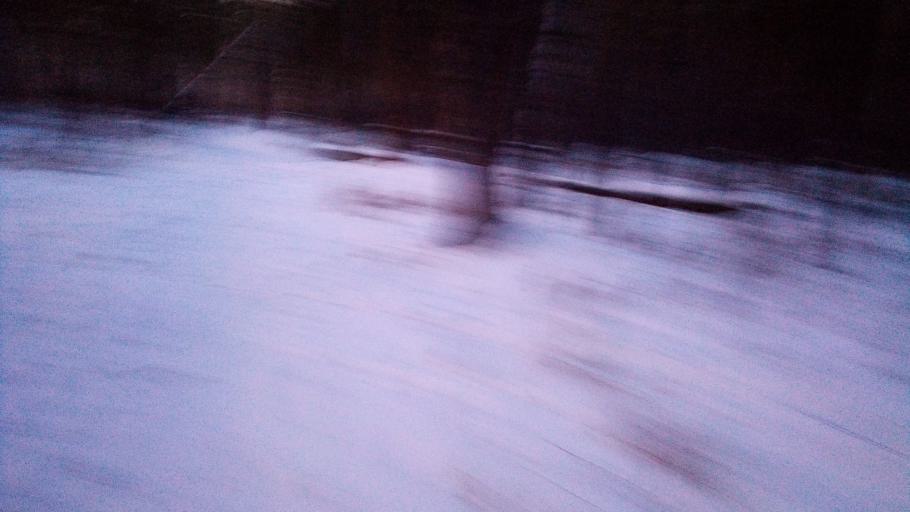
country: RU
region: Chelyabinsk
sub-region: Gorod Chelyabinsk
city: Chelyabinsk
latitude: 55.1641
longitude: 61.3317
